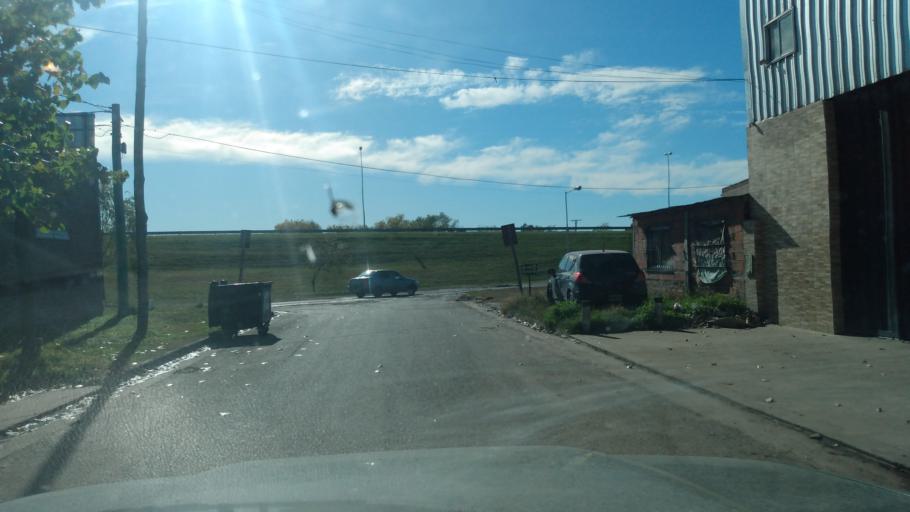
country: AR
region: Buenos Aires
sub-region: Partido de Lujan
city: Lujan
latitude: -34.5627
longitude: -59.0884
